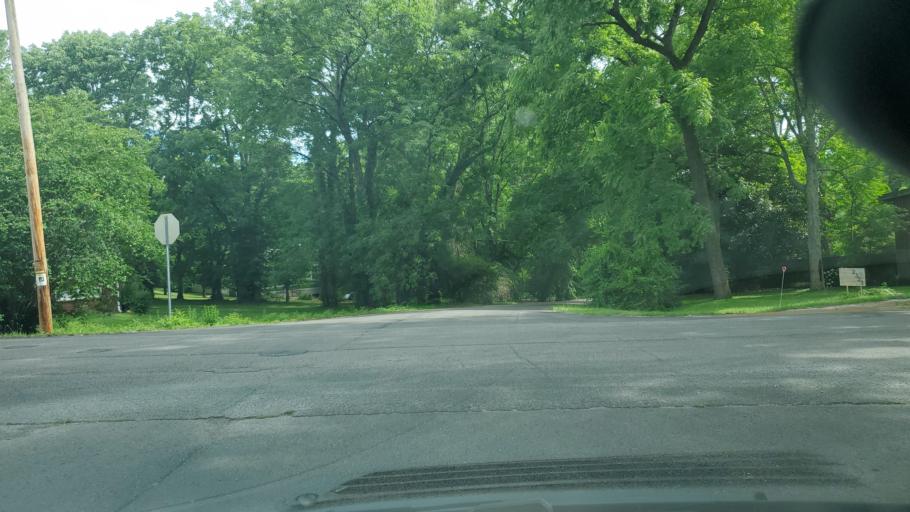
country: US
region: Tennessee
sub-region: Davidson County
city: Lakewood
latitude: 36.2000
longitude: -86.6810
